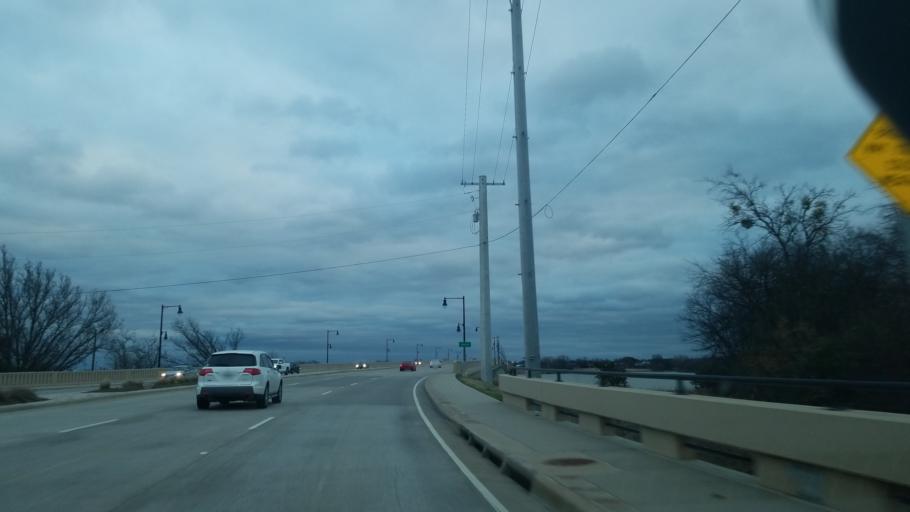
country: US
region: Texas
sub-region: Denton County
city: Little Elm
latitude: 33.1611
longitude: -96.9569
